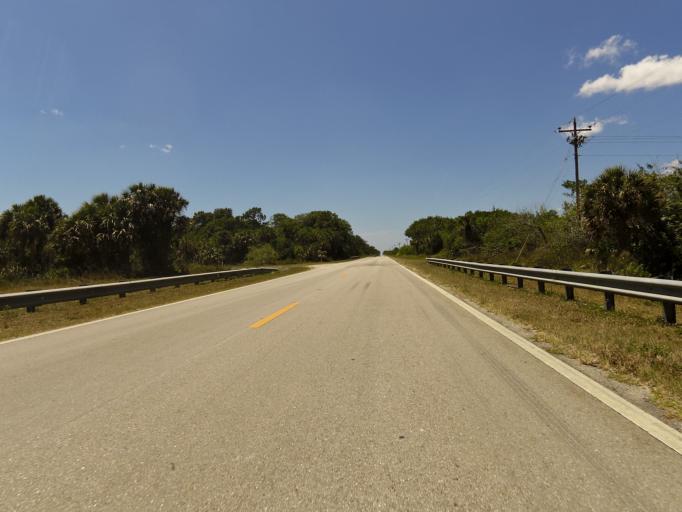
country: US
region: Florida
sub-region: Collier County
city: Immokalee
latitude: 26.2953
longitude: -81.3863
